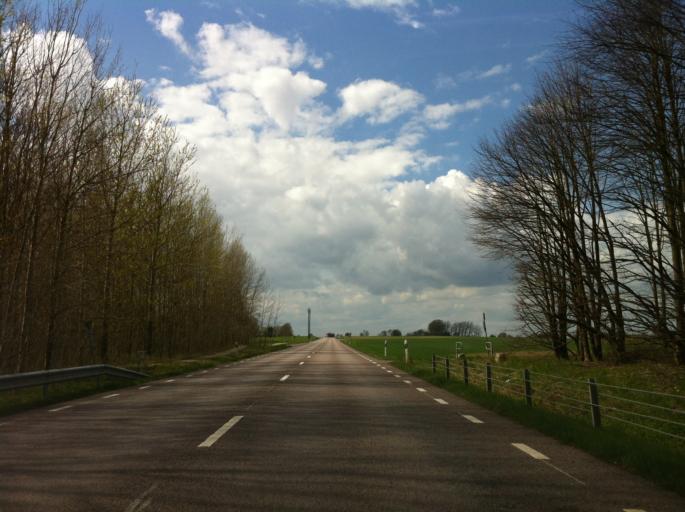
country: SE
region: Skane
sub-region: Eslovs Kommun
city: Stehag
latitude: 55.8539
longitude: 13.3856
